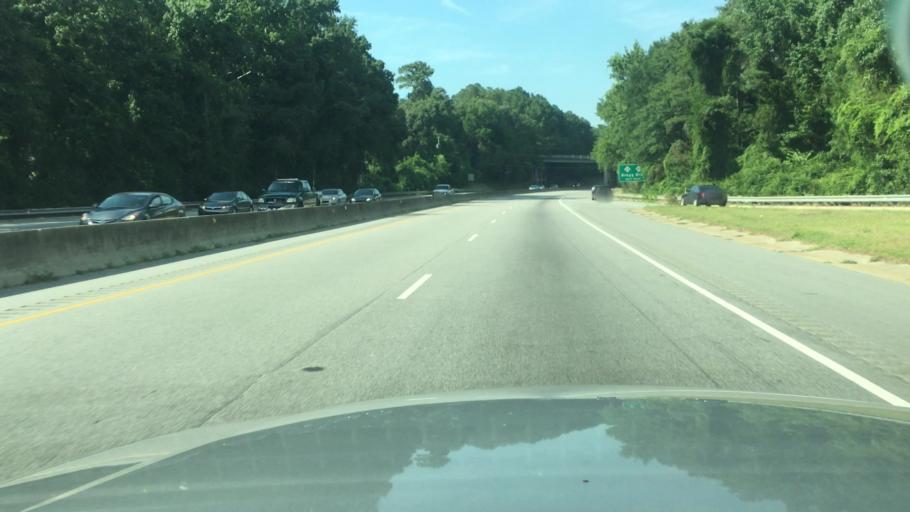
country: US
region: North Carolina
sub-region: Cumberland County
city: Fayetteville
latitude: 35.0584
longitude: -78.8929
